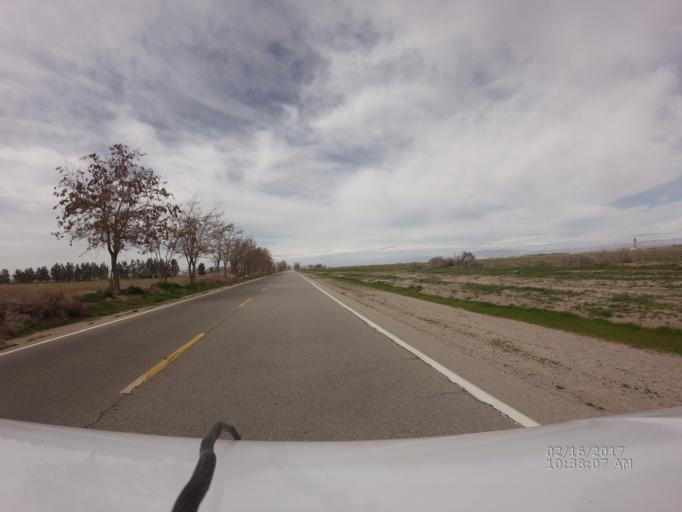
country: US
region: California
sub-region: Los Angeles County
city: Lancaster
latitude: 34.7193
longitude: -117.9996
